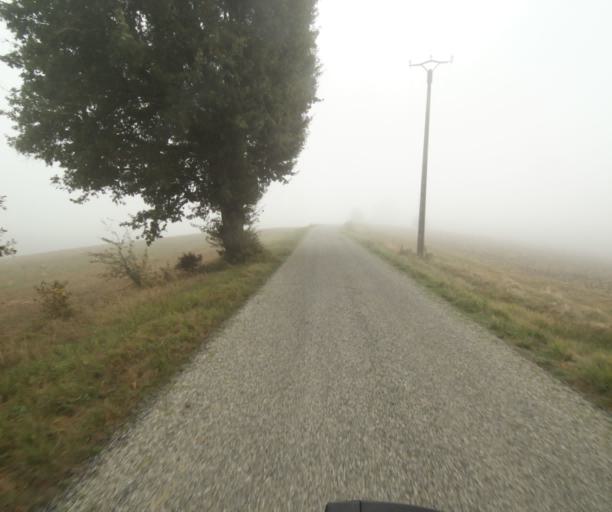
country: FR
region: Midi-Pyrenees
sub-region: Departement de la Haute-Garonne
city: Villemur-sur-Tarn
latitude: 43.8968
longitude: 1.4799
